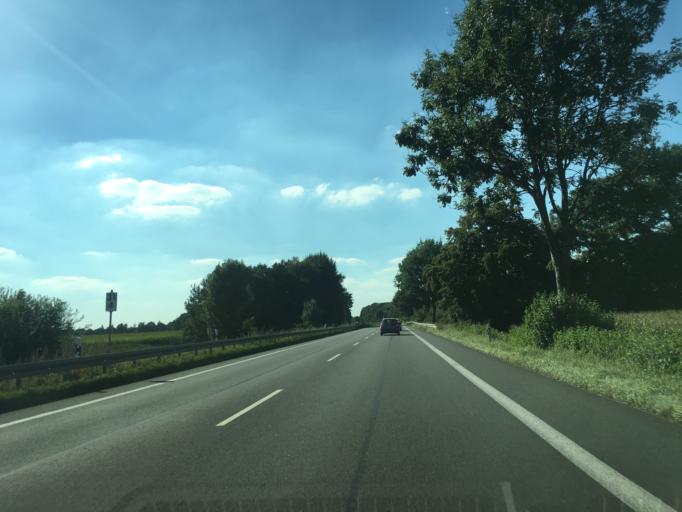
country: DE
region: North Rhine-Westphalia
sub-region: Regierungsbezirk Munster
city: Sassenberg
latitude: 51.9417
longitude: 8.0679
